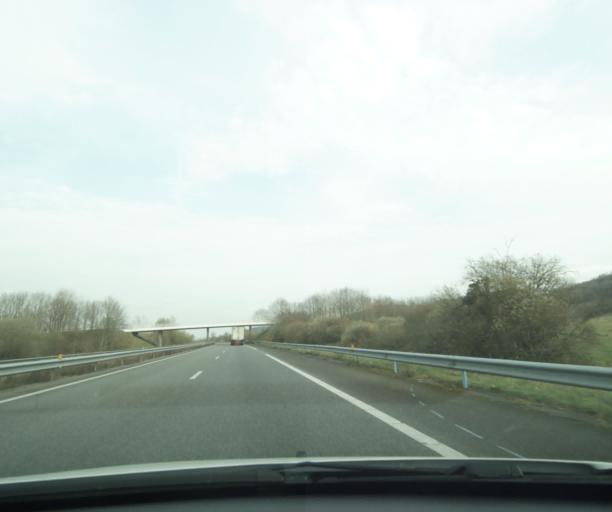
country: FR
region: Aquitaine
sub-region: Departement des Landes
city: Labatut
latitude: 43.5182
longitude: -0.9654
